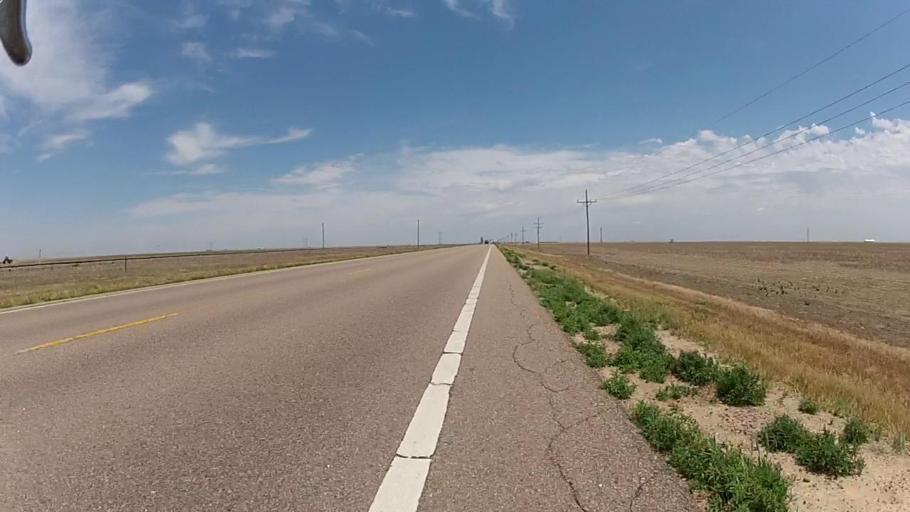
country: US
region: Kansas
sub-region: Haskell County
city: Sublette
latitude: 37.4669
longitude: -100.9026
